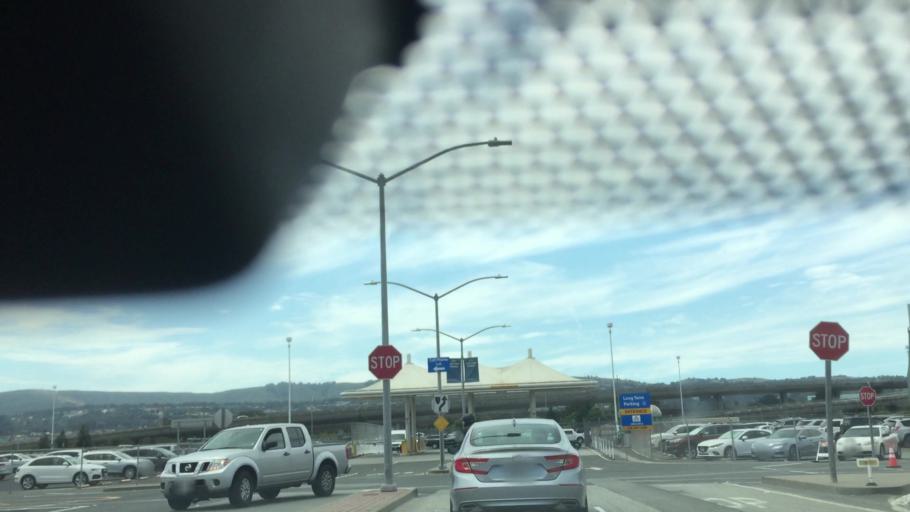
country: US
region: California
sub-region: San Mateo County
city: San Bruno
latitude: 37.6344
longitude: -122.4001
